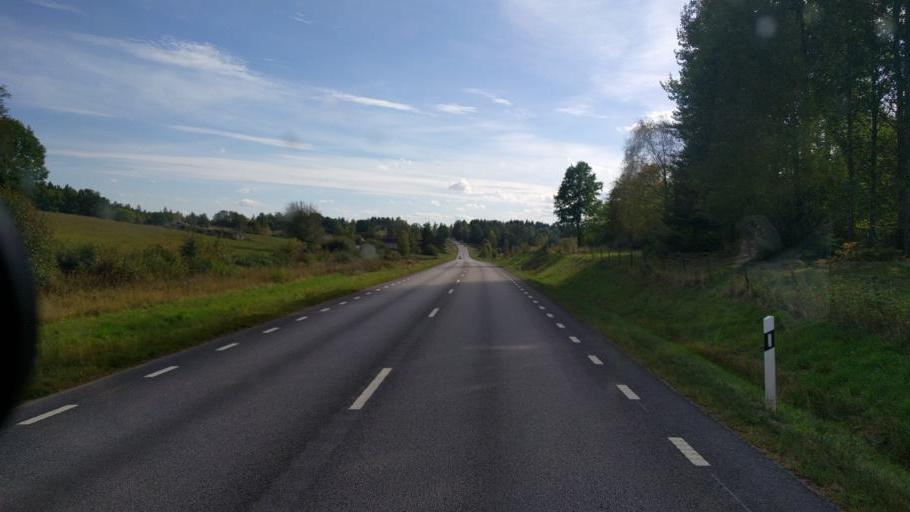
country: SE
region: OEstergoetland
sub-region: Kinda Kommun
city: Kisa
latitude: 57.9274
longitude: 15.6732
